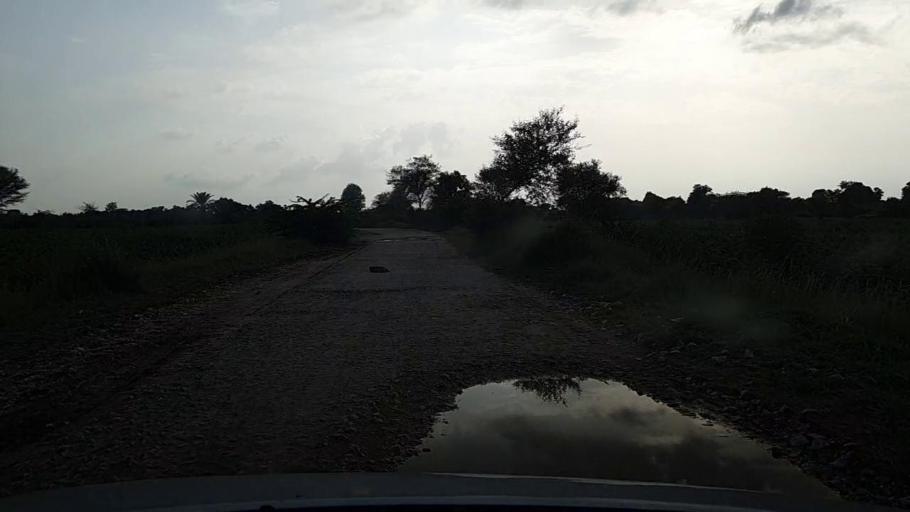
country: PK
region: Sindh
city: Pad Idan
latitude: 26.7944
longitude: 68.2281
